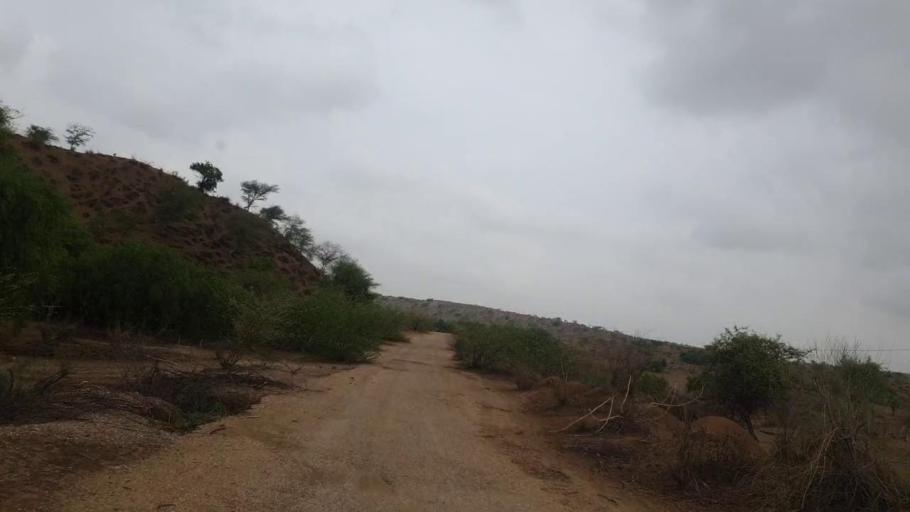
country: PK
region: Sindh
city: Diplo
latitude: 24.5128
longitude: 69.4973
